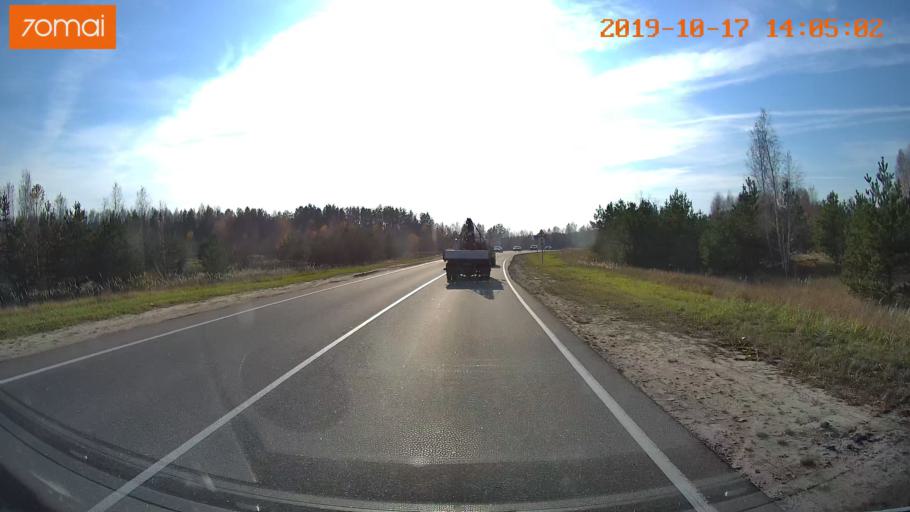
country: RU
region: Rjazan
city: Spas-Klepiki
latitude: 55.1197
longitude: 40.1317
